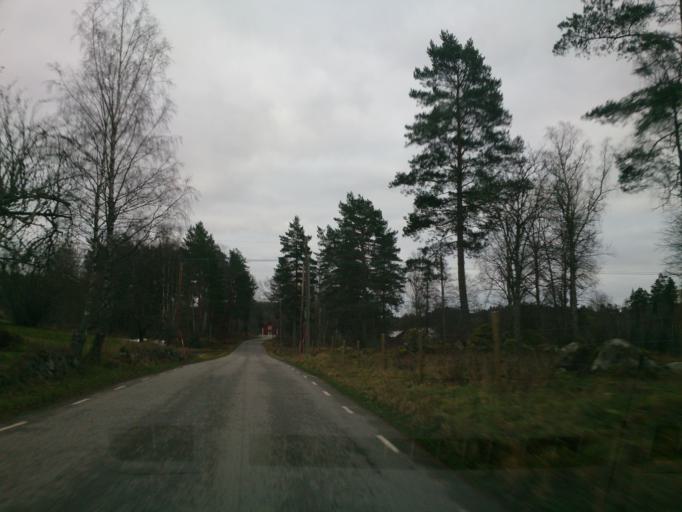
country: SE
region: OEstergoetland
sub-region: Atvidabergs Kommun
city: Atvidaberg
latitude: 58.3264
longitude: 16.0453
